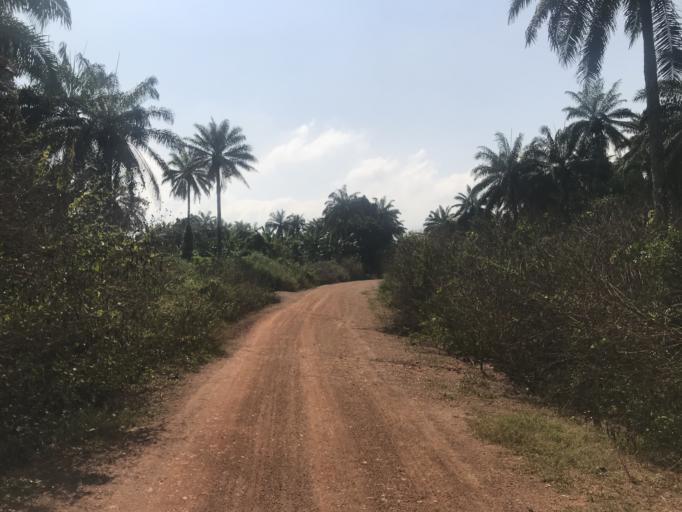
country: NG
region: Osun
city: Ikirun
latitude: 7.8307
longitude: 4.6383
